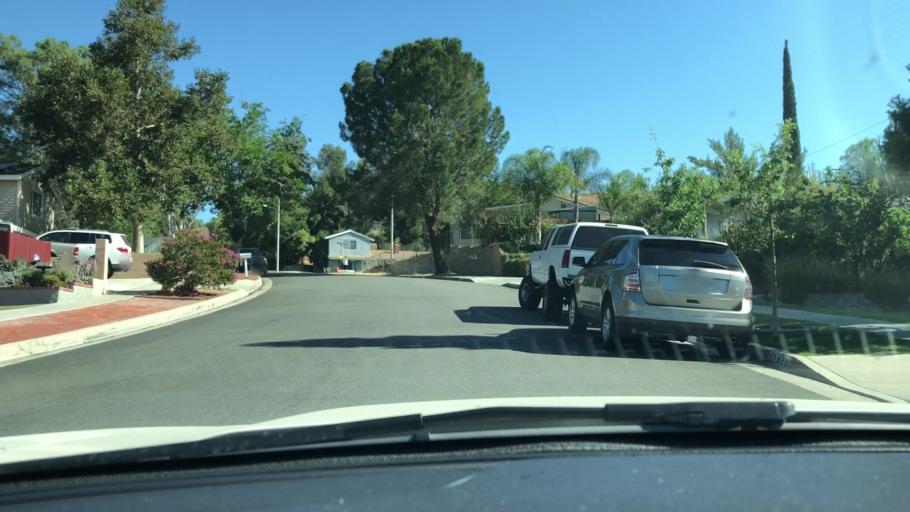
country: US
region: California
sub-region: Los Angeles County
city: Santa Clarita
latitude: 34.4192
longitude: -118.4443
